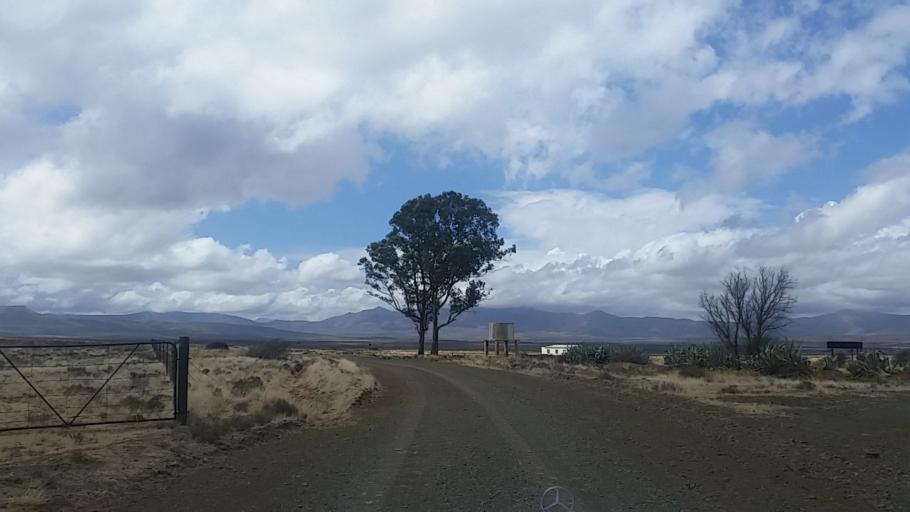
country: ZA
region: Eastern Cape
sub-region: Cacadu District Municipality
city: Graaff-Reinet
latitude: -31.9049
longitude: 24.7579
